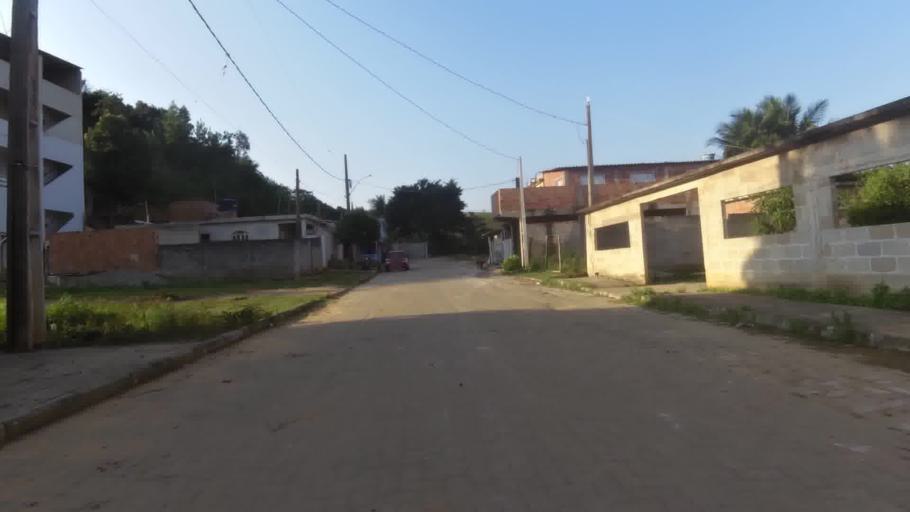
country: BR
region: Espirito Santo
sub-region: Piuma
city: Piuma
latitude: -20.8325
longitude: -40.7173
